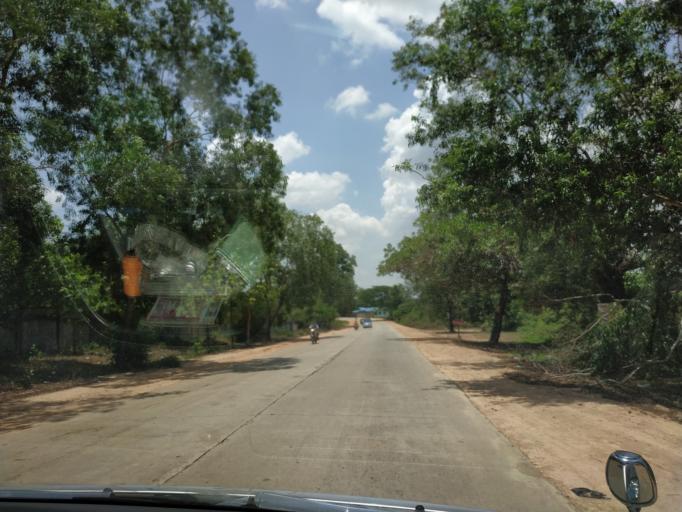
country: MM
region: Bago
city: Bago
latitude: 17.4704
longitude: 96.4669
